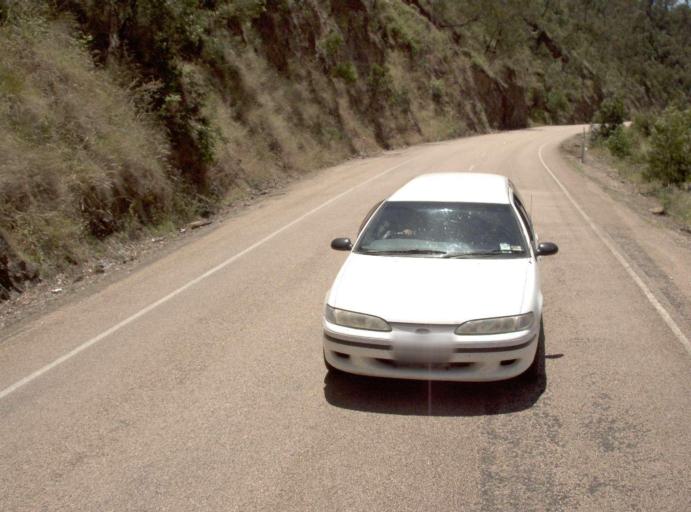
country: AU
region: Victoria
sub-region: East Gippsland
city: Bairnsdale
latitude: -37.4683
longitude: 147.8281
